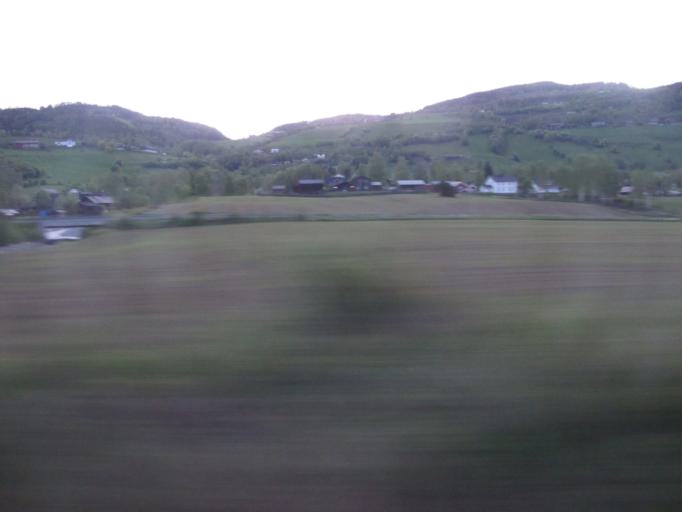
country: NO
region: Oppland
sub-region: Nord-Fron
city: Vinstra
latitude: 61.5857
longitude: 9.7791
